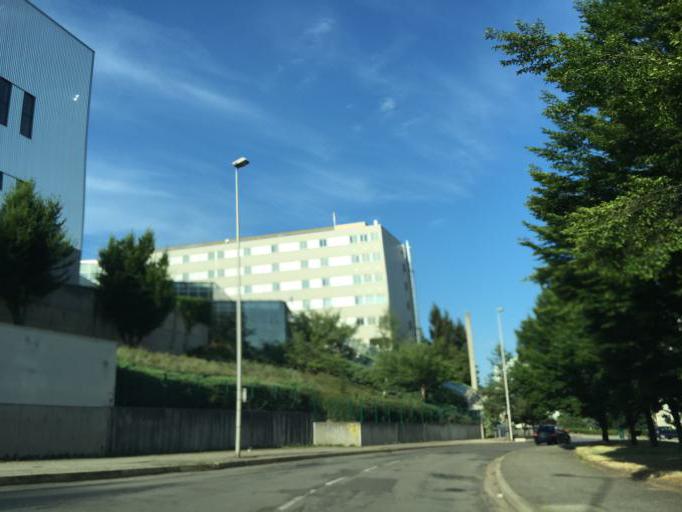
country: FR
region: Rhone-Alpes
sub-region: Departement de la Loire
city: Saint-Etienne
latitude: 45.4183
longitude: 4.4221
